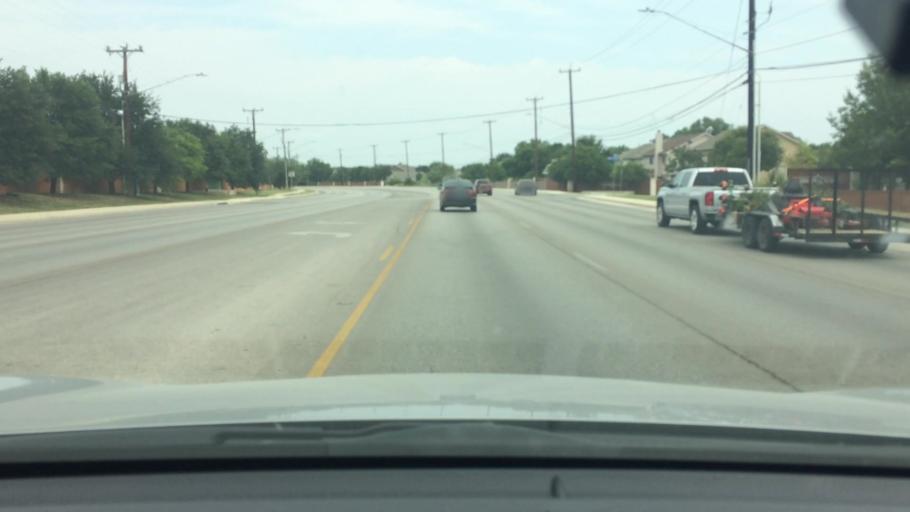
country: US
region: Texas
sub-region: Bexar County
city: Leon Valley
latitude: 29.4766
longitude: -98.6614
